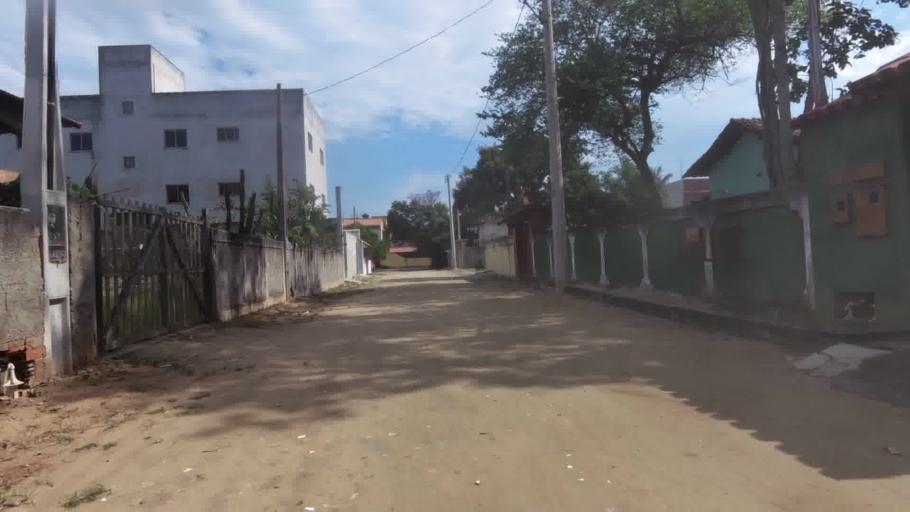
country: BR
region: Espirito Santo
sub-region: Piuma
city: Piuma
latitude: -20.8513
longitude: -40.7510
